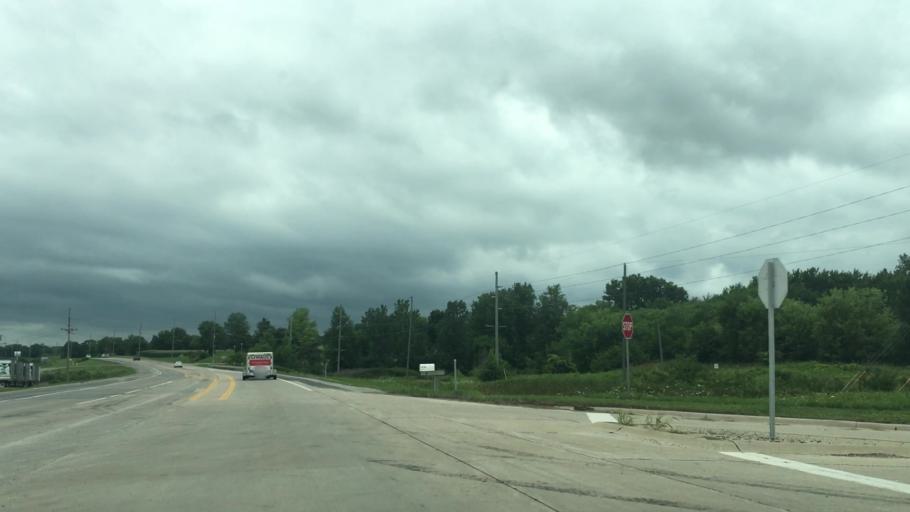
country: US
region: Iowa
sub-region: Johnson County
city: Tiffin
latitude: 41.7006
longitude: -91.6290
